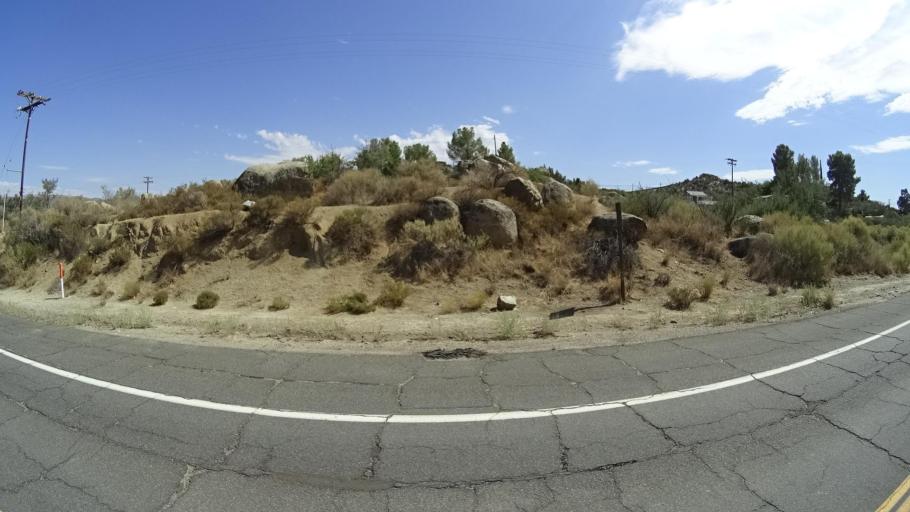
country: MX
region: Baja California
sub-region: Tecate
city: Cereso del Hongo
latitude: 32.6162
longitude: -116.1923
